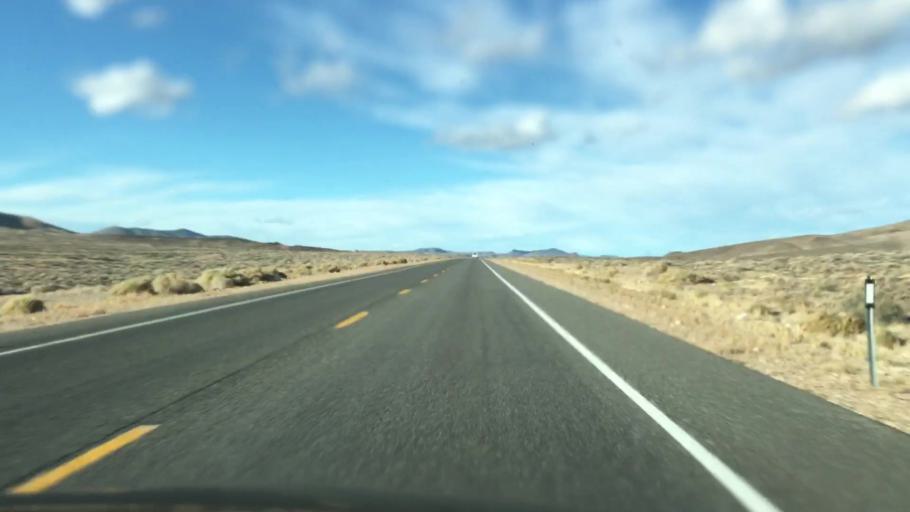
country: US
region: Nevada
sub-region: Esmeralda County
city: Goldfield
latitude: 37.5324
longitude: -117.1929
